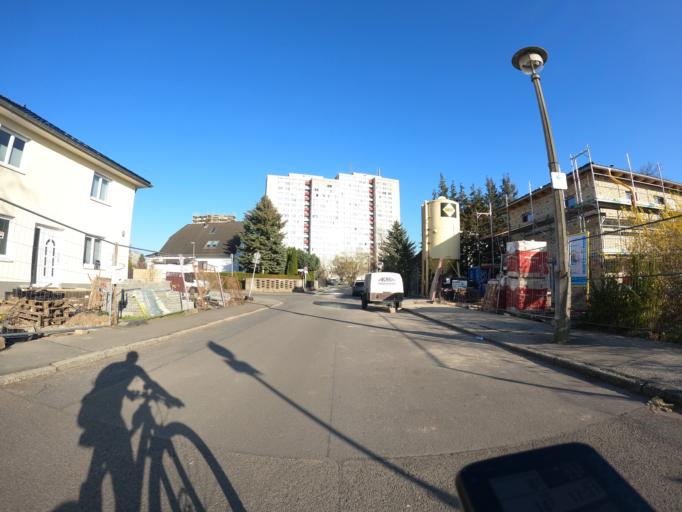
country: DE
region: Berlin
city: Marzahn
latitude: 52.5353
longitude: 13.5479
